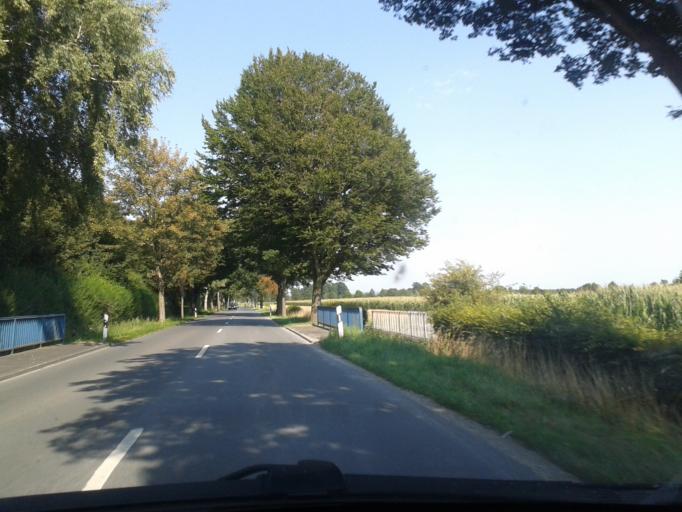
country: DE
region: North Rhine-Westphalia
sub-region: Regierungsbezirk Detmold
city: Hovelhof
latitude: 51.7363
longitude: 8.6490
